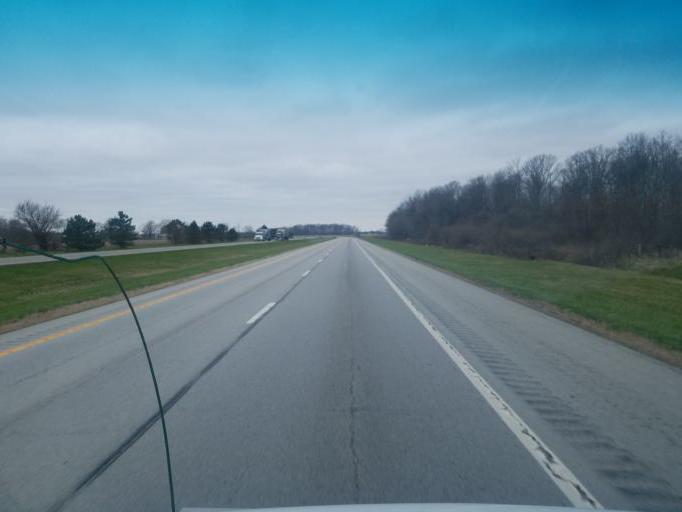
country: US
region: Ohio
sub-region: Allen County
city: Elida
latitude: 40.8367
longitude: -84.2240
